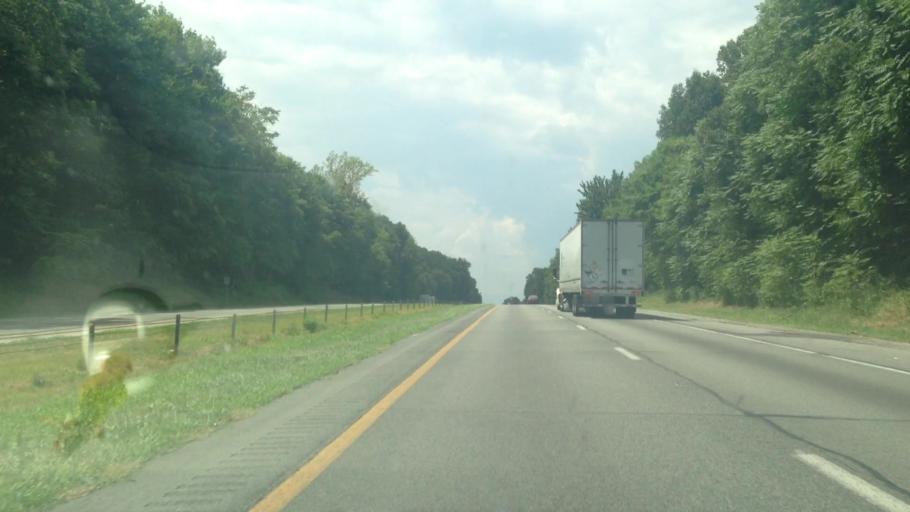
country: US
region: North Carolina
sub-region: Surry County
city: Pilot Mountain
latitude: 36.3483
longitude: -80.4651
